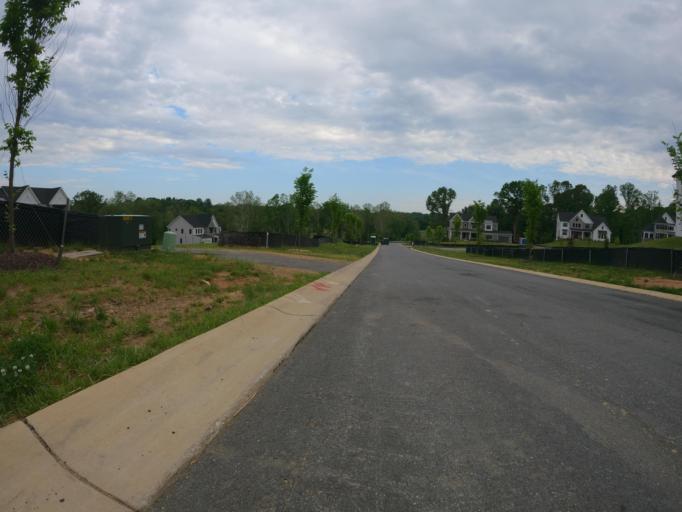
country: US
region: Maryland
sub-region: Howard County
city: Highland
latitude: 39.2266
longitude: -77.0001
